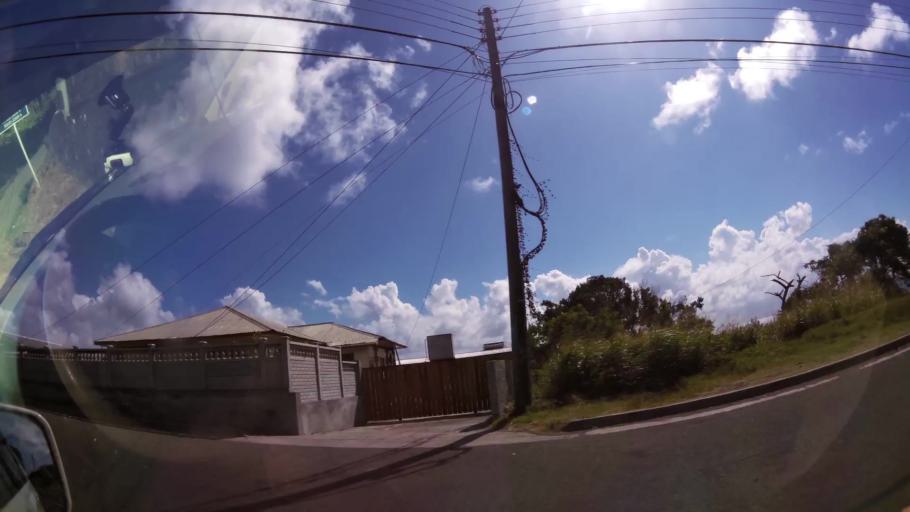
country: VC
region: Saint George
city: Kingstown
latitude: 13.1288
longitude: -61.1919
